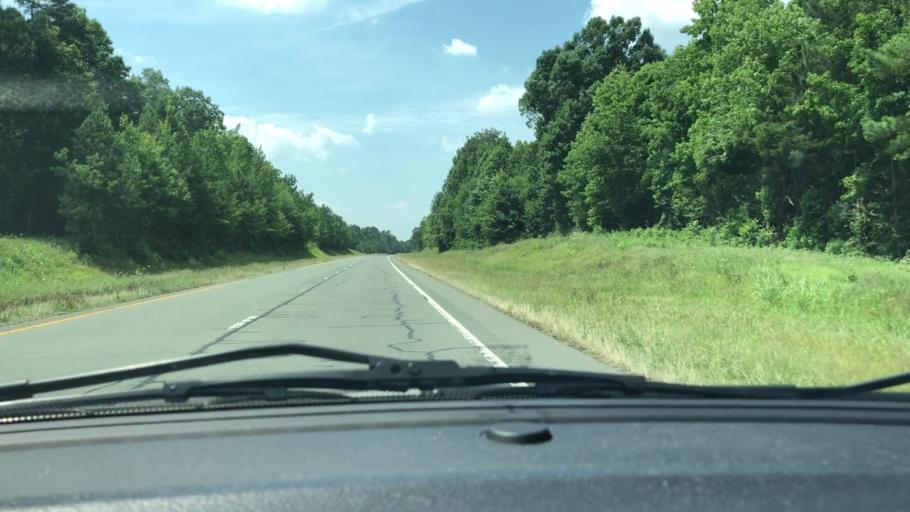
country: US
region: North Carolina
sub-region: Chatham County
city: Siler City
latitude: 35.7824
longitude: -79.5119
